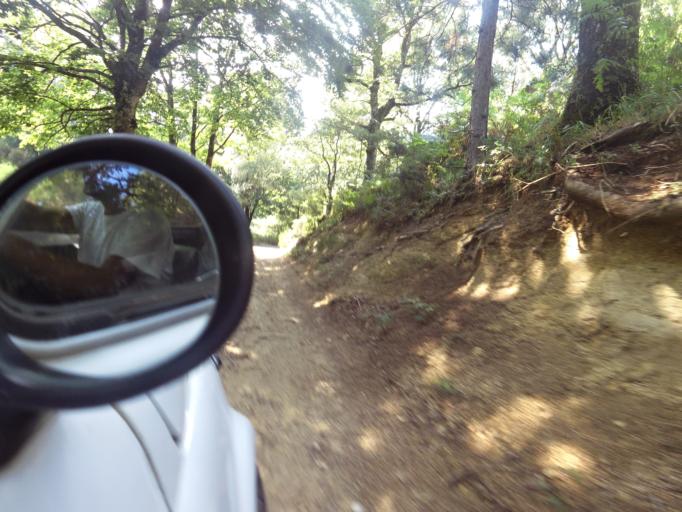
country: IT
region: Calabria
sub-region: Provincia di Vibo-Valentia
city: Nardodipace
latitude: 38.5104
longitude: 16.3877
